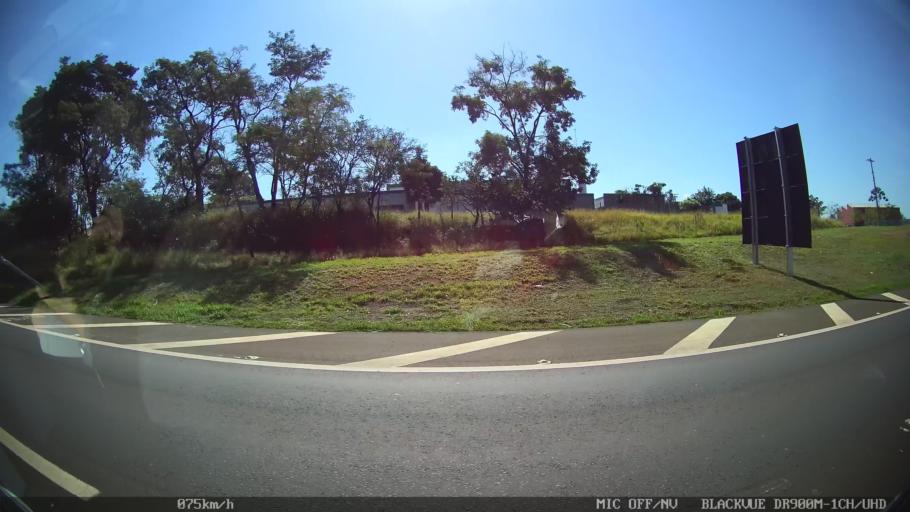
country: BR
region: Sao Paulo
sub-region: Franca
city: Franca
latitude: -20.5577
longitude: -47.4414
